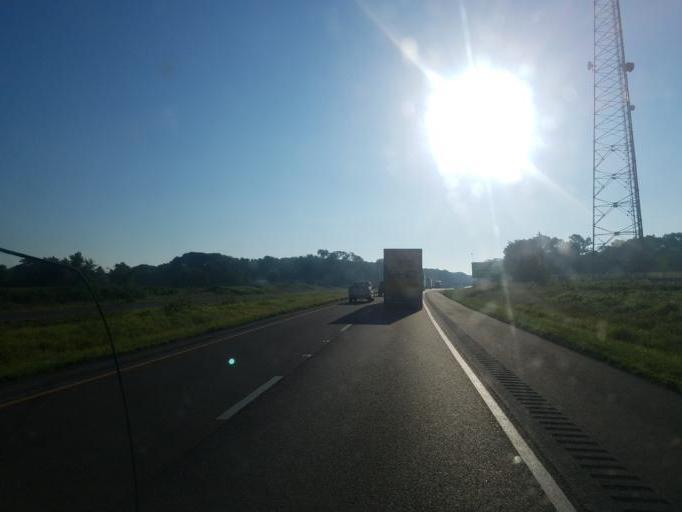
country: US
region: Illinois
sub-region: Bond County
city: Greenville
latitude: 38.9132
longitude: -89.2764
